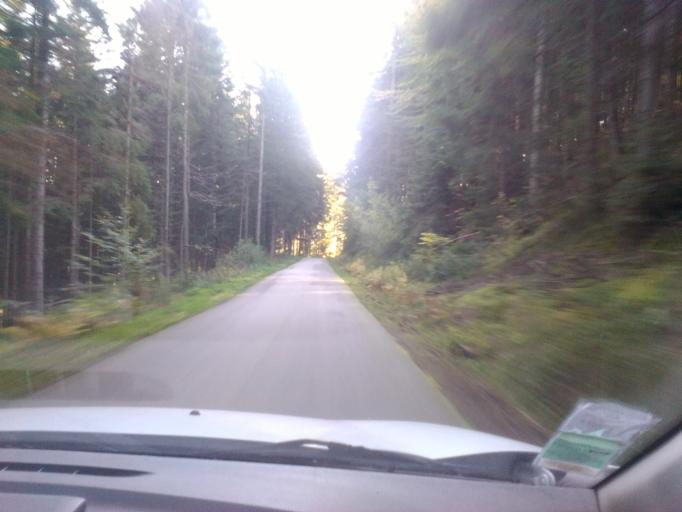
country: FR
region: Lorraine
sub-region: Departement des Vosges
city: Taintrux
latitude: 48.2296
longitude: 6.8784
